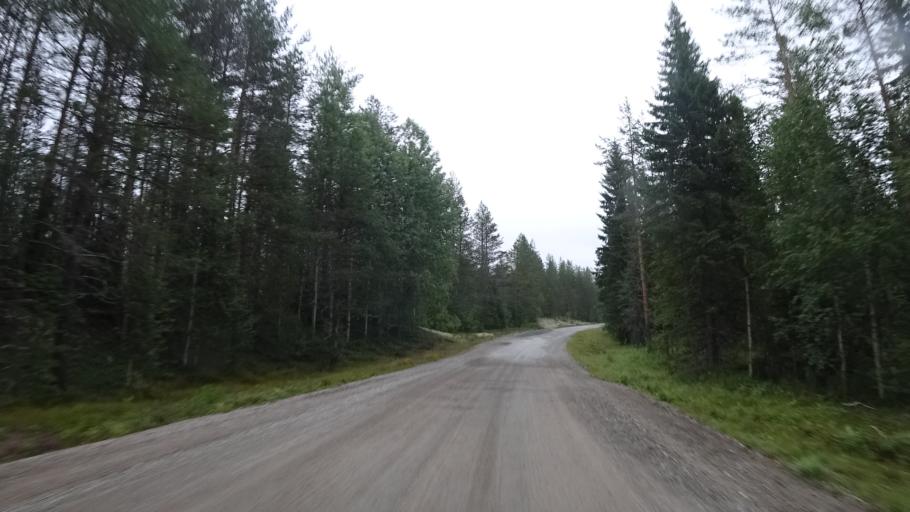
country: FI
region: North Karelia
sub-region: Joensuu
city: Ilomantsi
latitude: 63.2290
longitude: 30.8075
